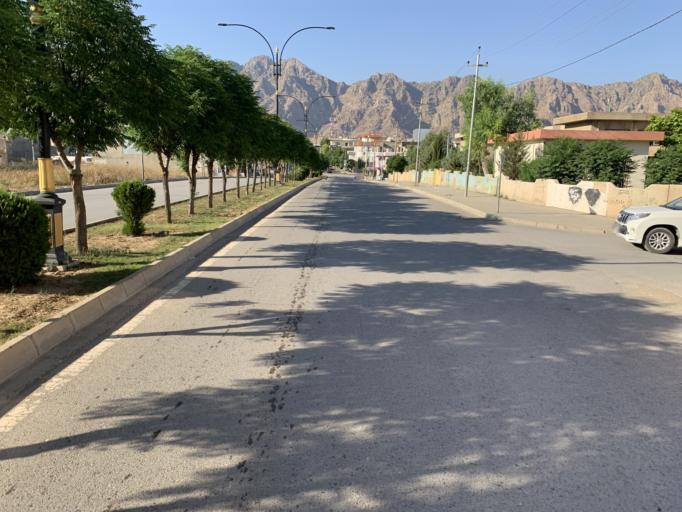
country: IQ
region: As Sulaymaniyah
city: Raniye
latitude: 36.2457
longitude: 44.8744
